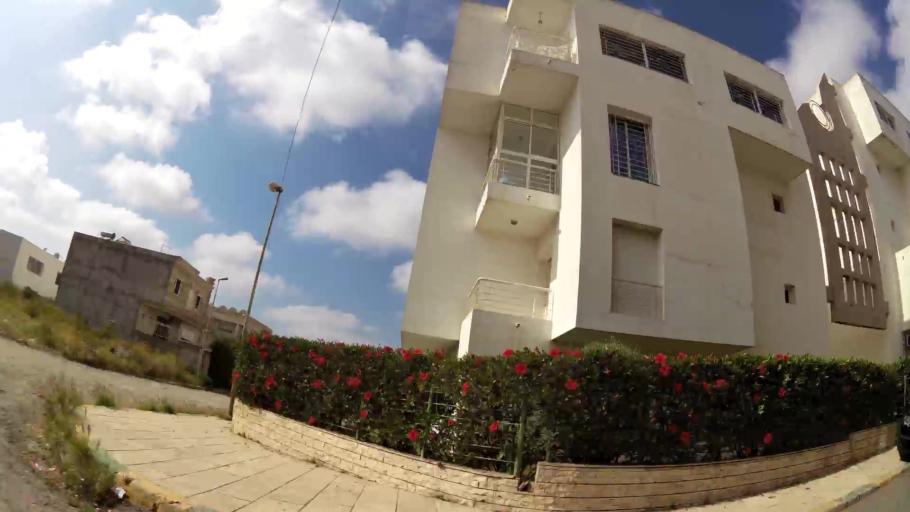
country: MA
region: Rabat-Sale-Zemmour-Zaer
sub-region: Skhirate-Temara
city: Temara
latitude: 33.9483
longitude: -6.8741
